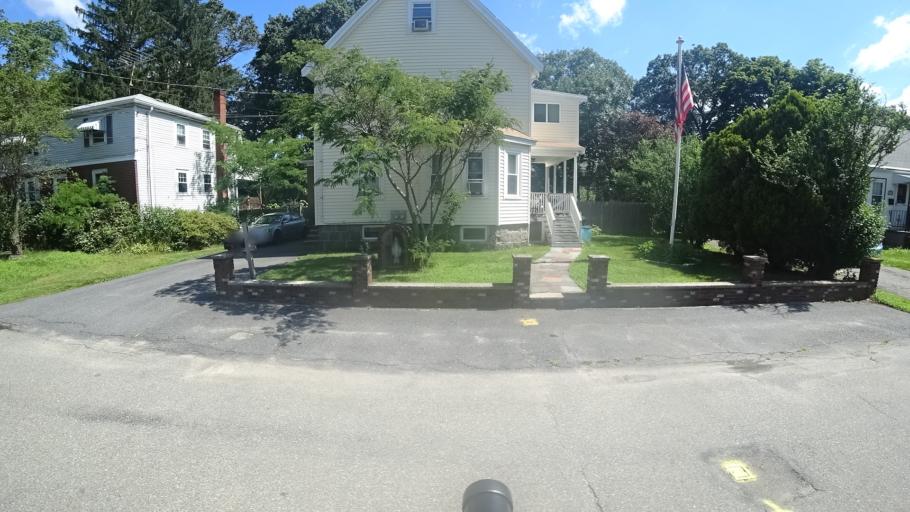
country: US
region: Massachusetts
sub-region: Norfolk County
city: Dedham
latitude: 42.2572
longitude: -71.1510
